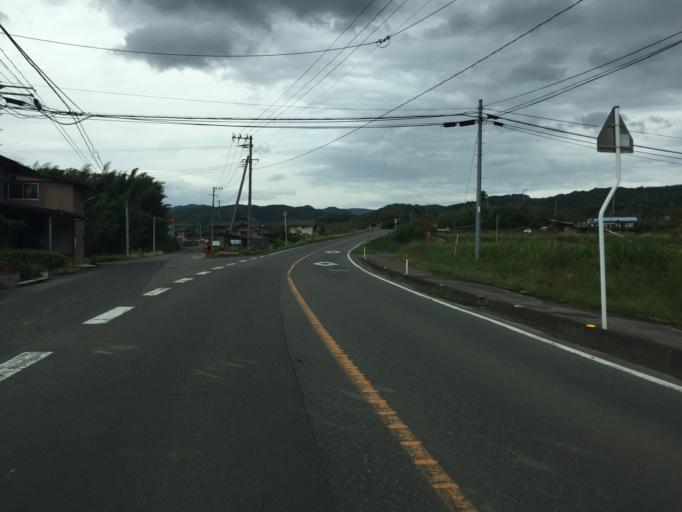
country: JP
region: Fukushima
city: Yanagawamachi-saiwaicho
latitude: 37.8663
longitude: 140.6193
